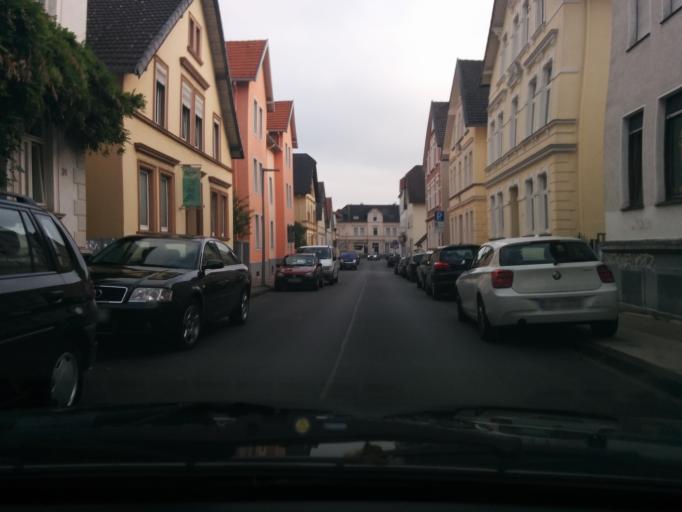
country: DE
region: North Rhine-Westphalia
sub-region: Regierungsbezirk Detmold
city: Bielefeld
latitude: 52.0299
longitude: 8.5229
